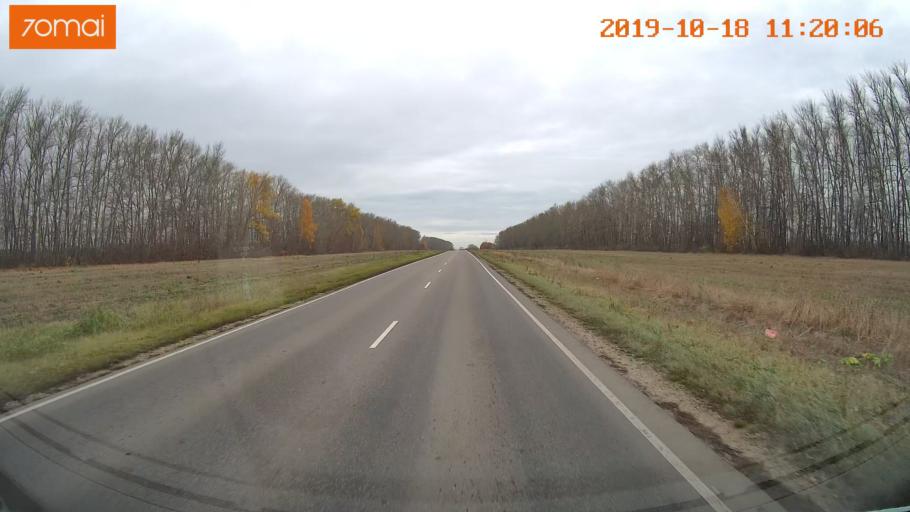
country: RU
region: Tula
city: Kimovsk
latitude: 54.0554
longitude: 38.5570
